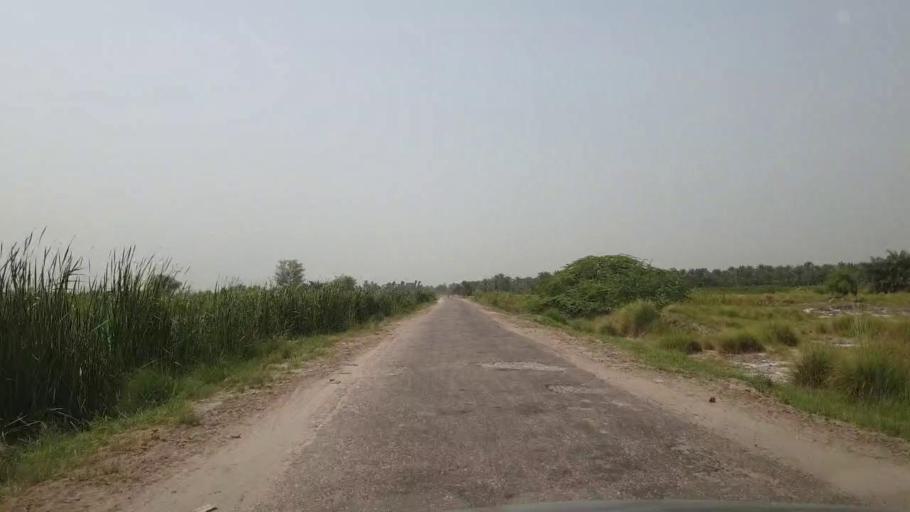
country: PK
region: Sindh
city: Gambat
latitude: 27.3852
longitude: 68.5486
